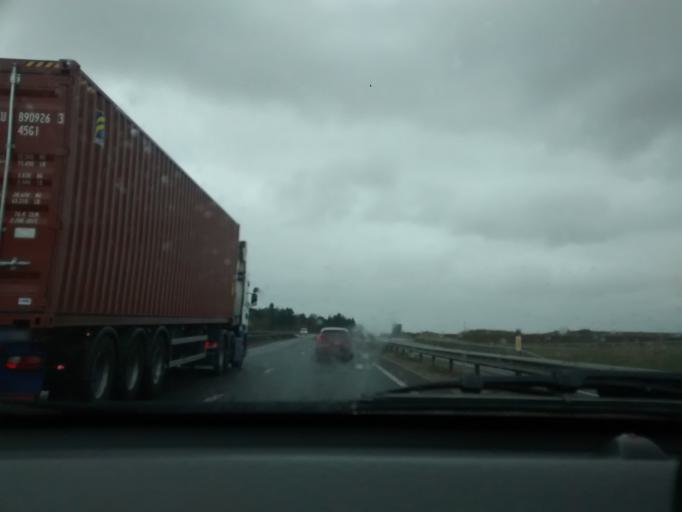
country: GB
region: England
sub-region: Suffolk
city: Stowmarket
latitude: 52.2047
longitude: 0.9773
